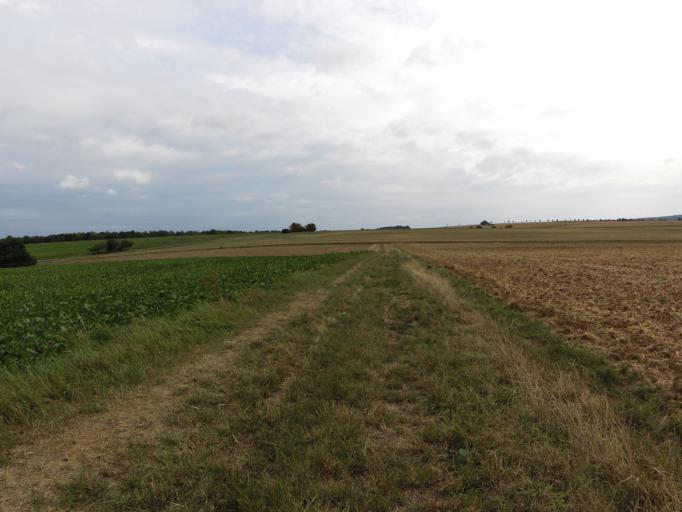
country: DE
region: Bavaria
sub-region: Regierungsbezirk Unterfranken
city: Rimpar
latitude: 49.8375
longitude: 9.9402
